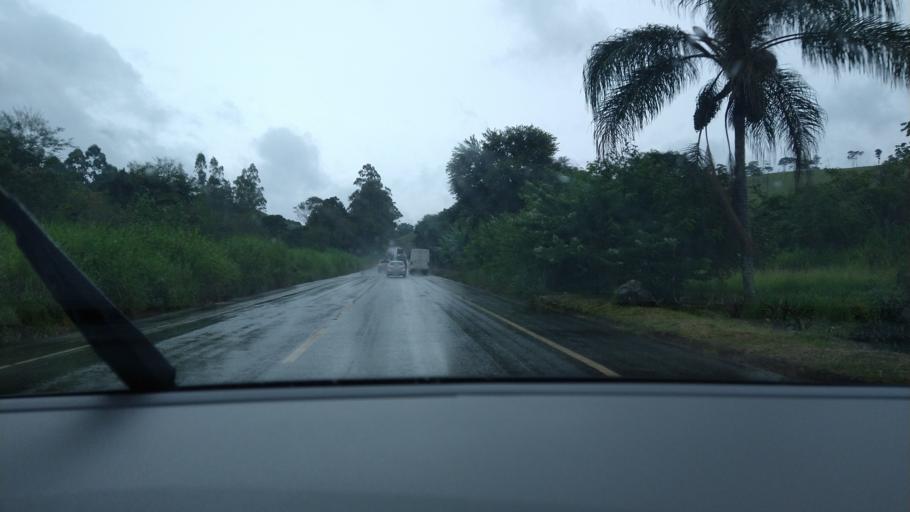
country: BR
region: Minas Gerais
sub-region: Vicosa
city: Vicosa
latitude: -20.6226
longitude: -42.8690
